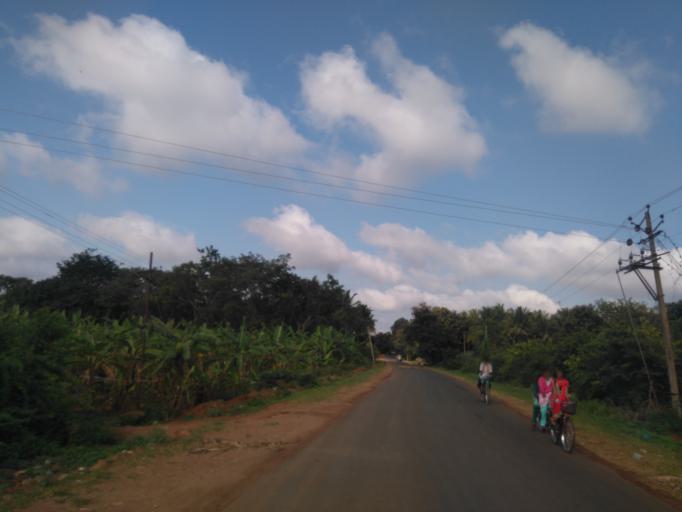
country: IN
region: Karnataka
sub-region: Mysore
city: Tirumakudal Narsipur
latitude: 12.2585
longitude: 76.9691
